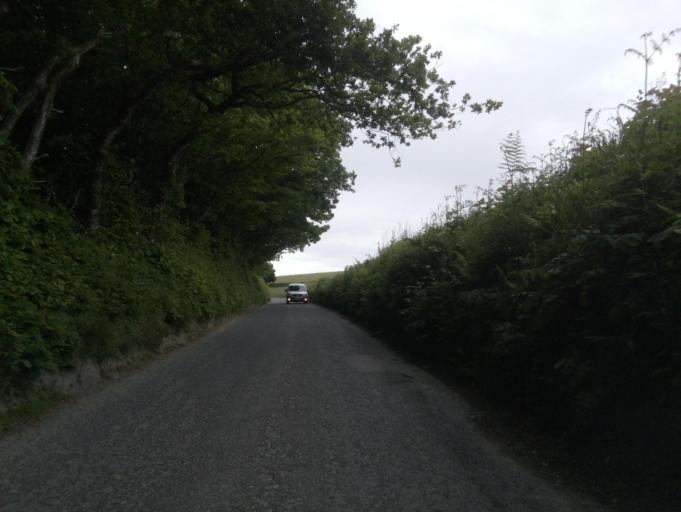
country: GB
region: England
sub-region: Devon
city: Dartmouth
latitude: 50.3316
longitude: -3.6468
